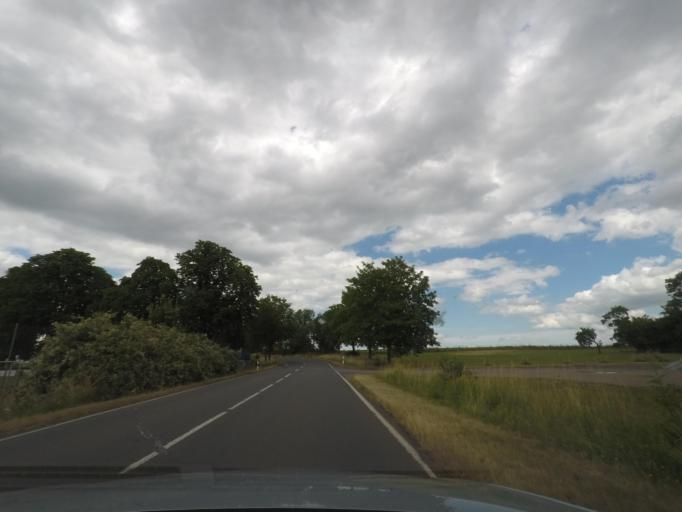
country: DE
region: Saxony-Anhalt
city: Ausleben
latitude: 52.0673
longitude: 11.0807
